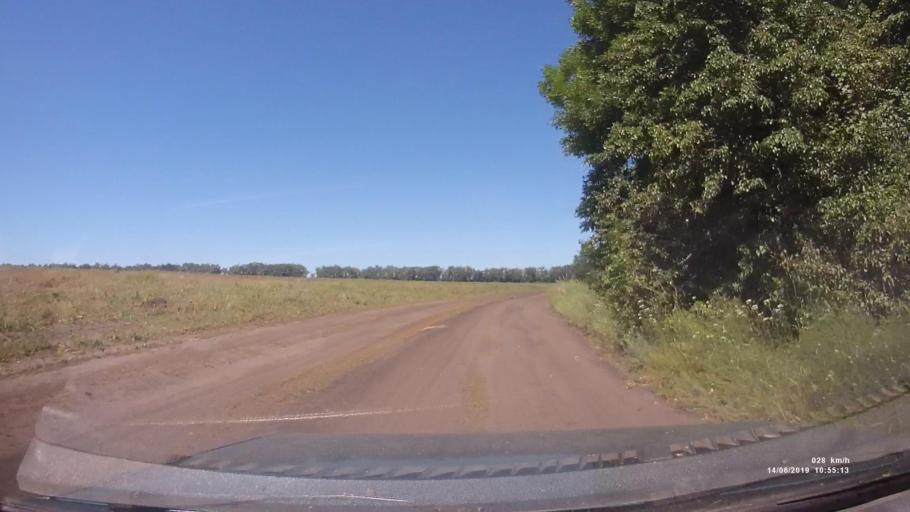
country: RU
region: Rostov
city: Kazanskaya
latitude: 49.8627
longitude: 41.3731
